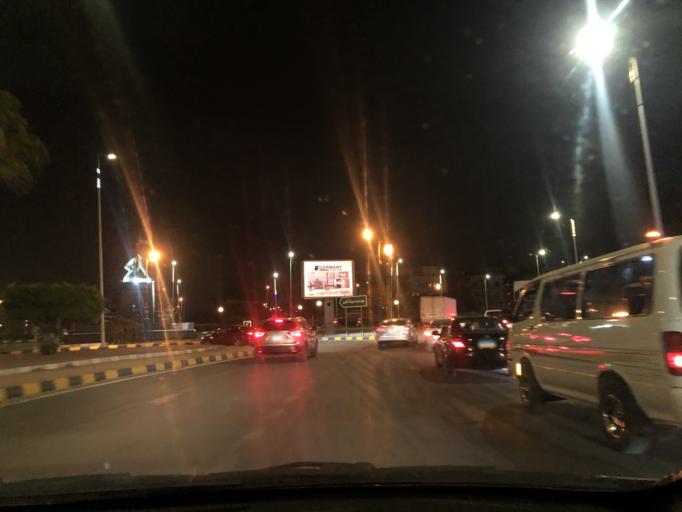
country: EG
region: Al Jizah
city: Madinat Sittah Uktubar
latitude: 29.9786
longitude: 30.9545
